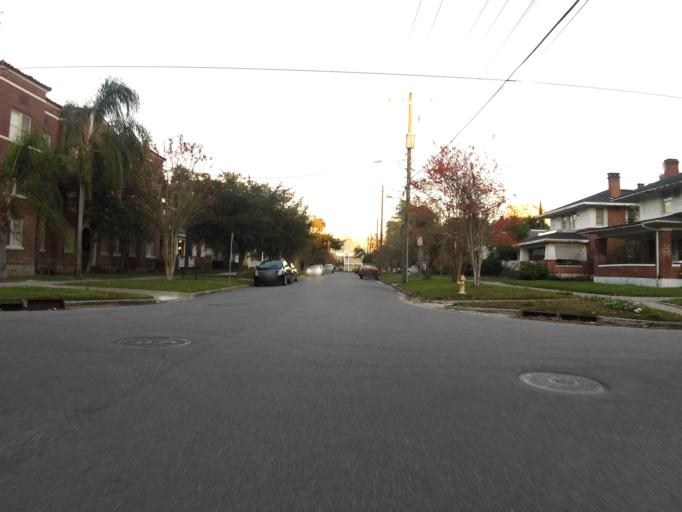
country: US
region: Florida
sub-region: Duval County
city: Jacksonville
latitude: 30.3143
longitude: -81.6835
